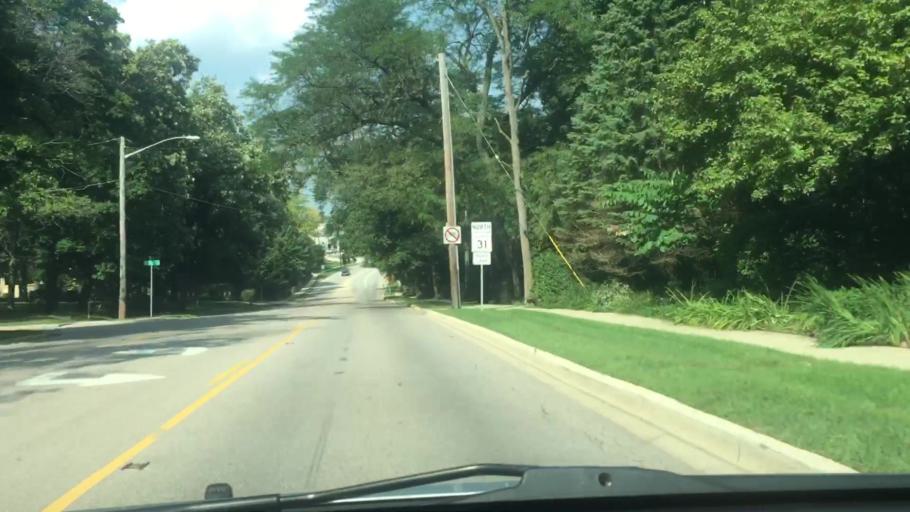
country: US
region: Illinois
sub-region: Kane County
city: Geneva
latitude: 41.8781
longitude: -88.3109
